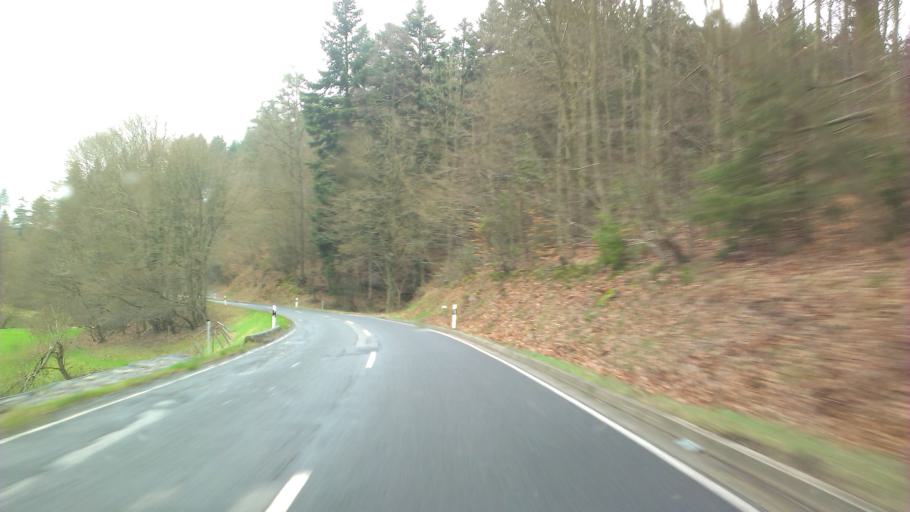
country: DE
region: Baden-Wuerttemberg
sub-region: Karlsruhe Region
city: Heiligkreuzsteinach
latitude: 49.5010
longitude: 8.7854
